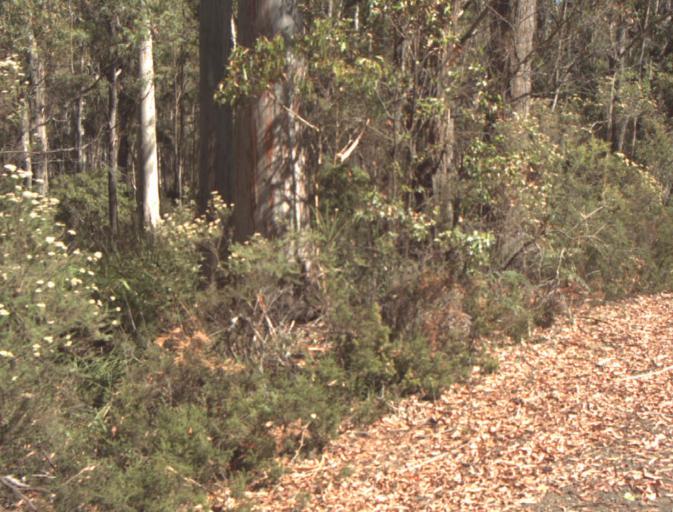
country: AU
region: Tasmania
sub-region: Launceston
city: Newstead
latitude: -41.3055
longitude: 147.3343
